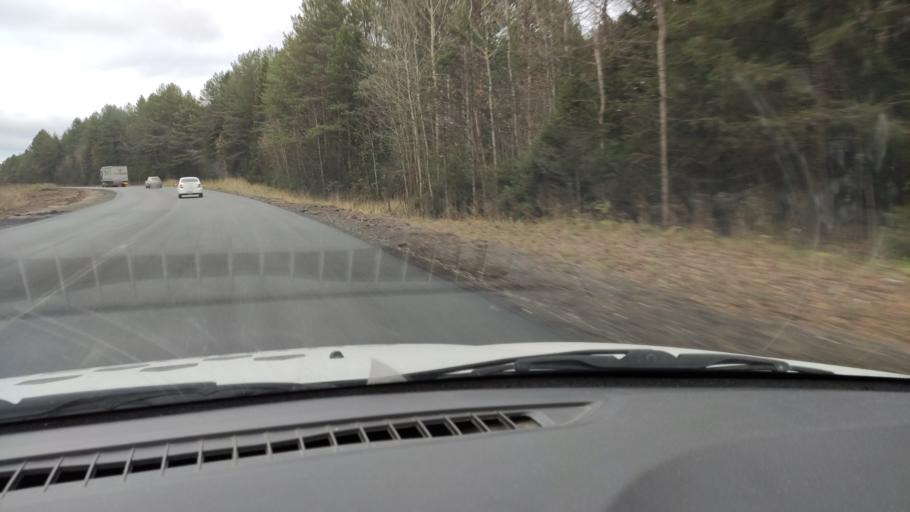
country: RU
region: Kirov
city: Slobodskoy
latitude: 58.7815
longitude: 50.4828
